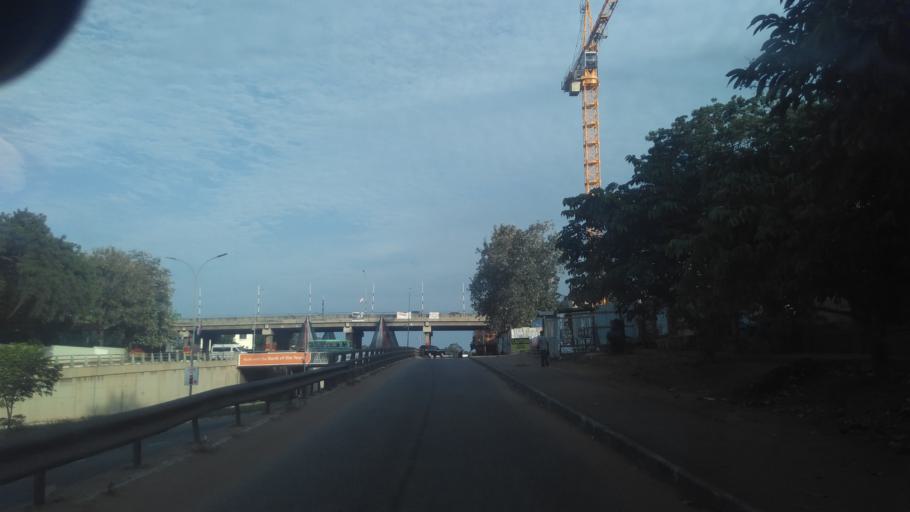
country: GH
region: Greater Accra
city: Accra
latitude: 5.5726
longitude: -0.1916
